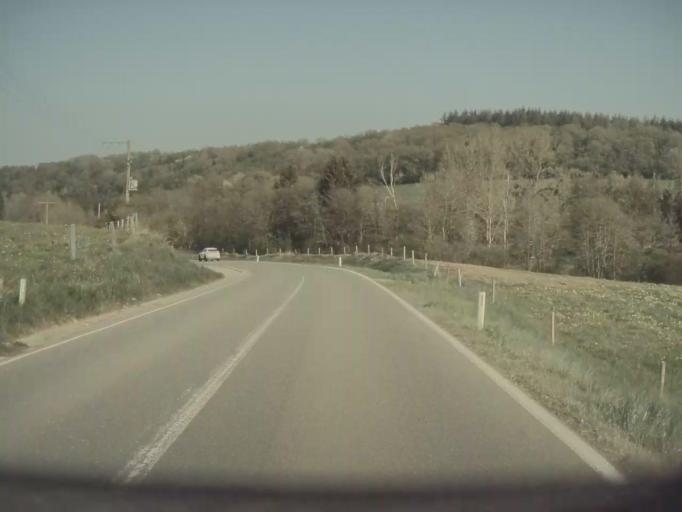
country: BE
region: Wallonia
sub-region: Province de Namur
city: Somme-Leuze
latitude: 50.3404
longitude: 5.3904
